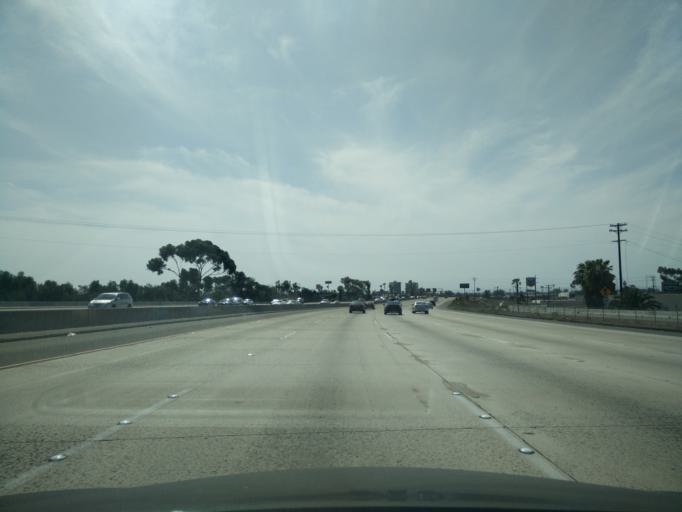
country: US
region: California
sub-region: San Diego County
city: National City
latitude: 32.6862
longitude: -117.1130
